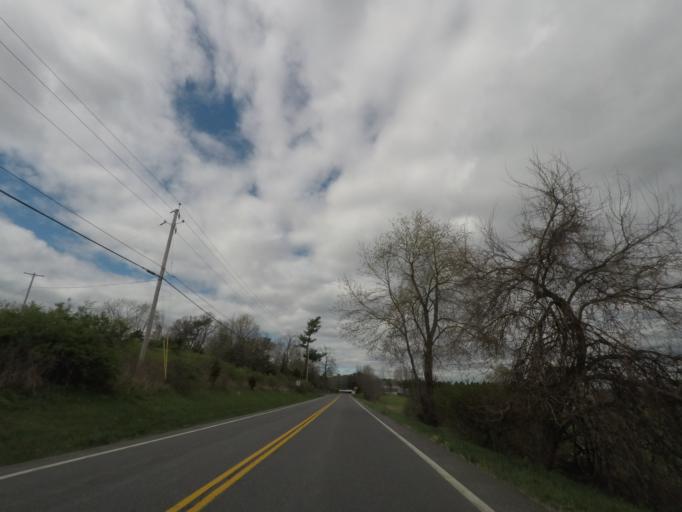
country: US
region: New York
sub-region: Columbia County
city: Philmont
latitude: 42.2755
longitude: -73.6609
